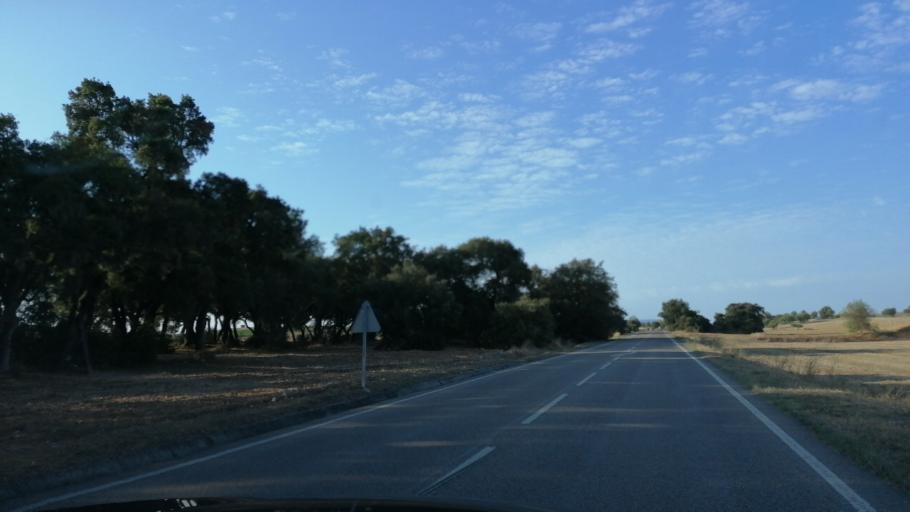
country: PT
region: Santarem
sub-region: Santarem
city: Santarem
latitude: 39.3246
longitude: -8.6630
